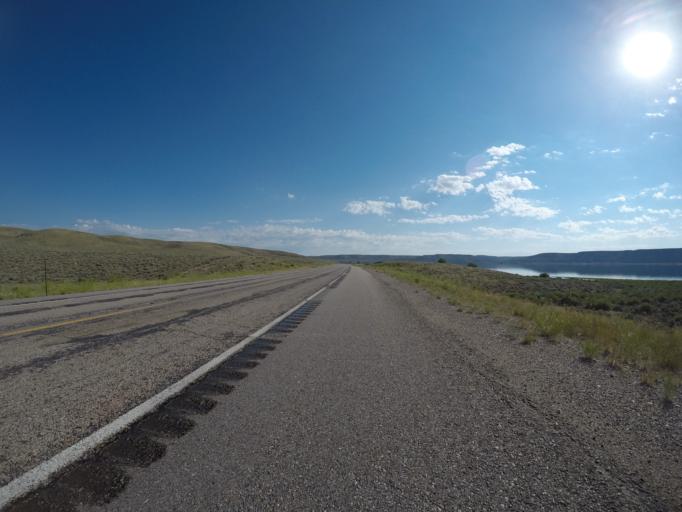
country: US
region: Wyoming
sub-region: Sublette County
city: Marbleton
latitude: 42.0935
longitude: -110.1480
